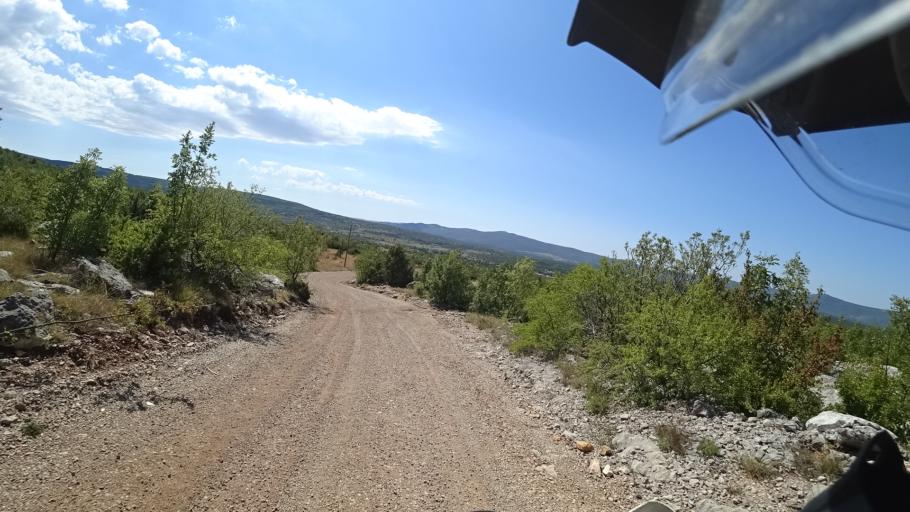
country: HR
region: Splitsko-Dalmatinska
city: Hrvace
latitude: 43.7537
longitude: 16.4473
